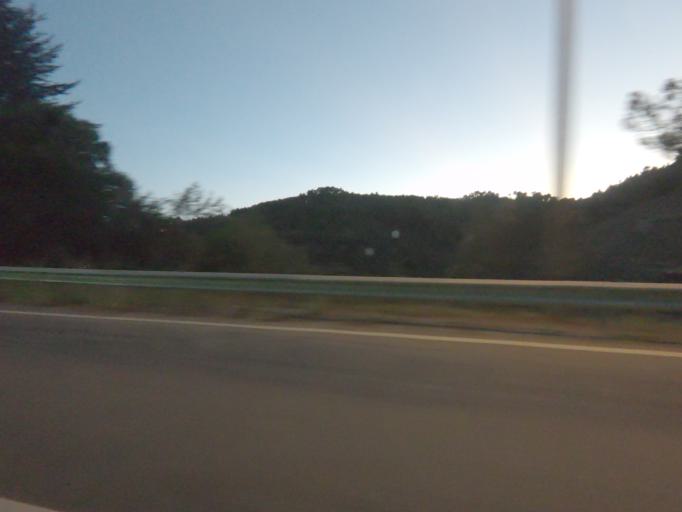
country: PT
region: Vila Real
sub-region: Vila Real
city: Vila Real
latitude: 41.2505
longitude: -7.6885
